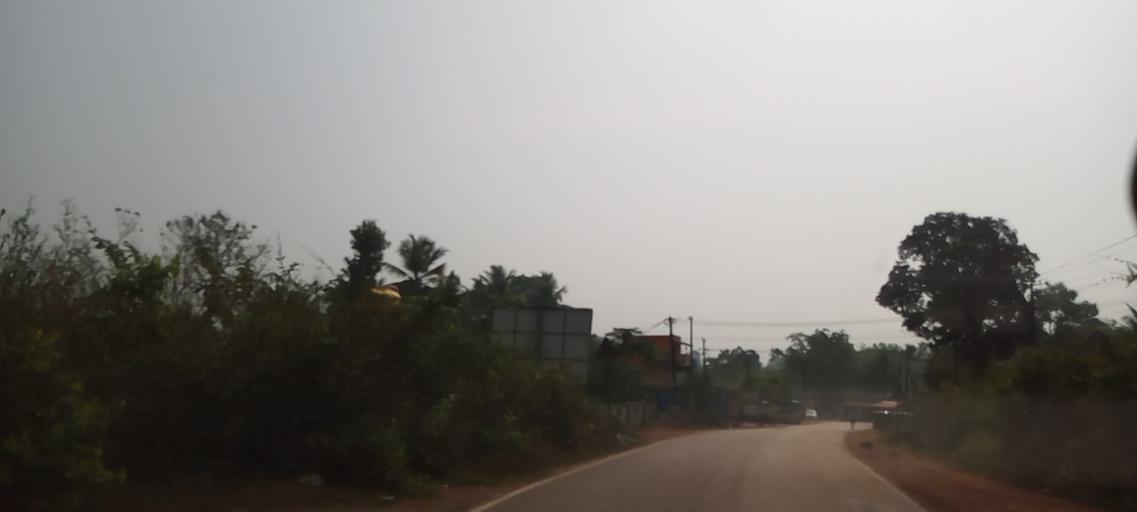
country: IN
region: Karnataka
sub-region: Udupi
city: Manipala
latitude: 13.5129
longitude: 74.8371
